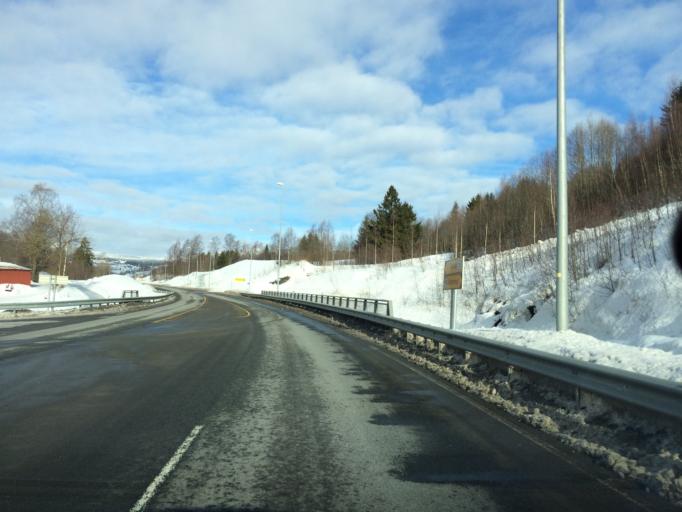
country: NO
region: Oppland
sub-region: Gausdal
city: Segalstad bru
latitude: 61.1901
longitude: 10.3176
